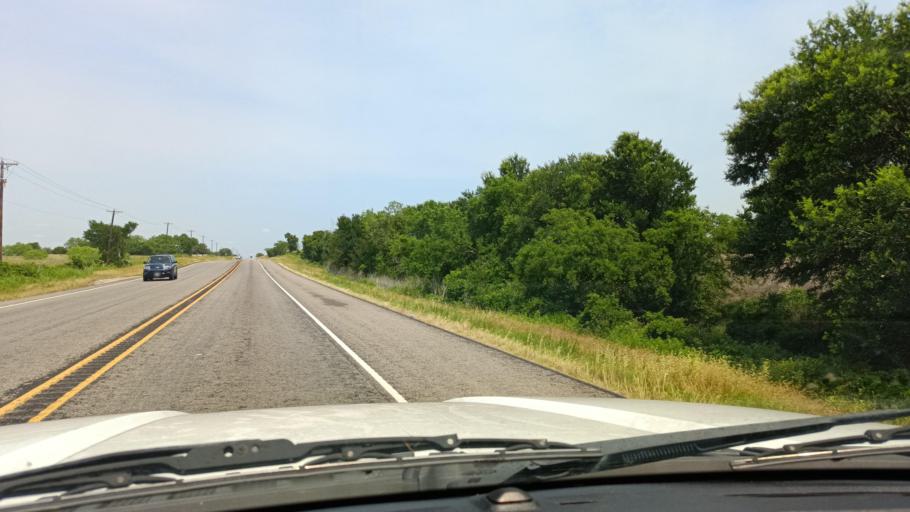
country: US
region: Texas
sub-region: Milam County
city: Cameron
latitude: 30.8488
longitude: -97.0625
